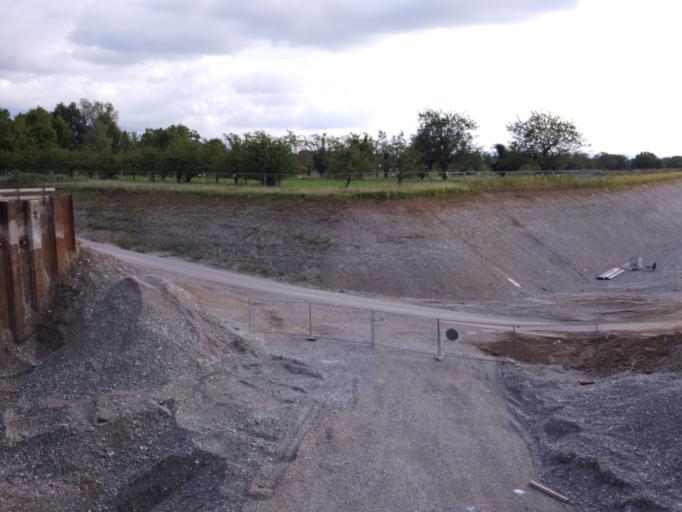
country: DE
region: Baden-Wuerttemberg
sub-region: Freiburg Region
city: Eimeldingen
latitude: 47.6207
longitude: 7.6035
